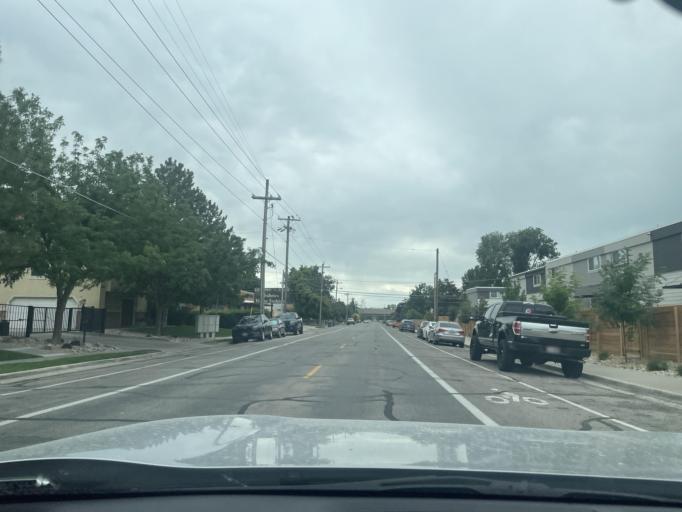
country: US
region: Utah
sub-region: Salt Lake County
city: South Salt Lake
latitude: 40.7222
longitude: -111.8768
